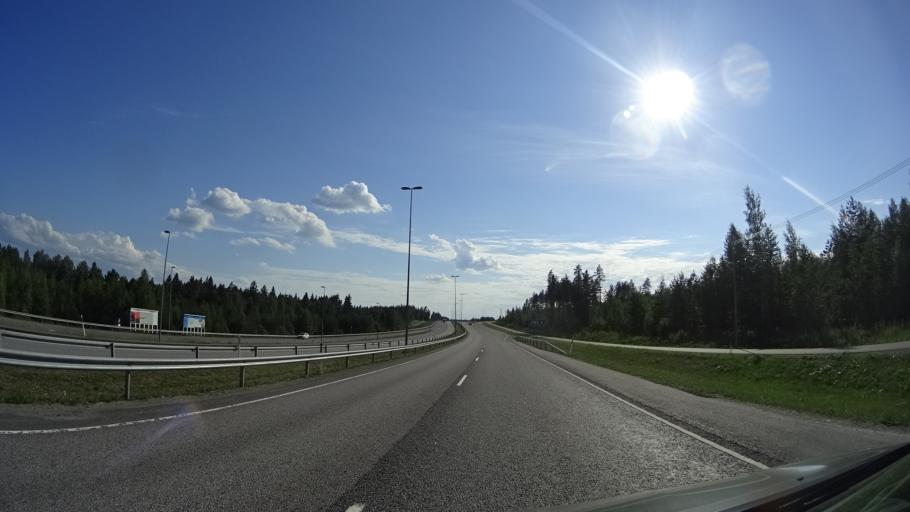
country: FI
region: South Karelia
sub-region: Imatra
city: Imatra
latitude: 61.1566
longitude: 28.6359
